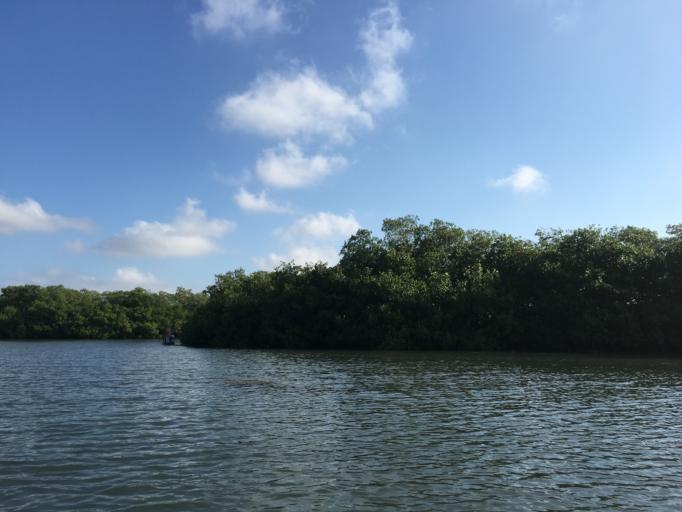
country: CO
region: Bolivar
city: Cartagena
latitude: 10.4852
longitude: -75.4824
